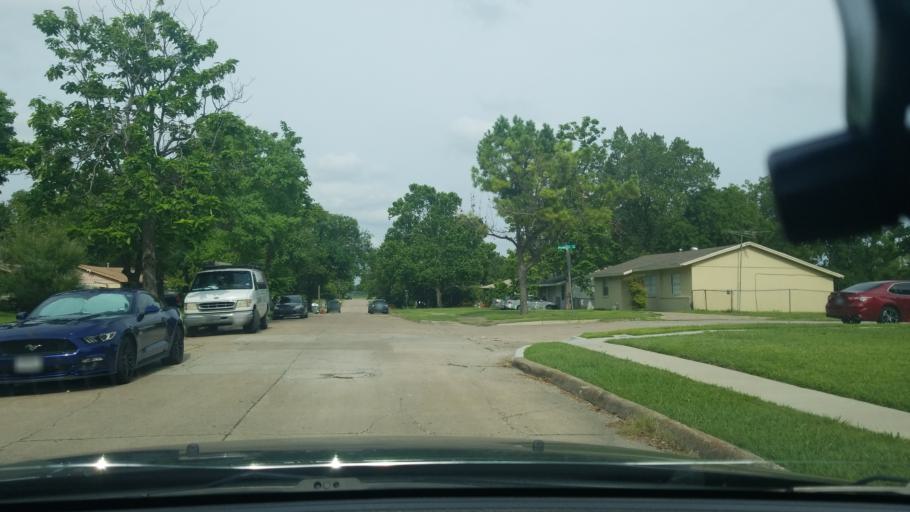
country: US
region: Texas
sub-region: Dallas County
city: Mesquite
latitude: 32.7600
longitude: -96.6262
